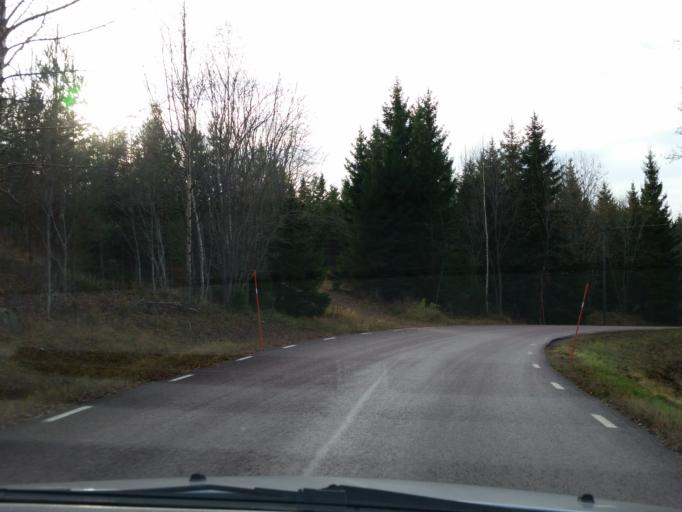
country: AX
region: Alands landsbygd
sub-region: Saltvik
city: Saltvik
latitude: 60.3420
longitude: 20.1066
